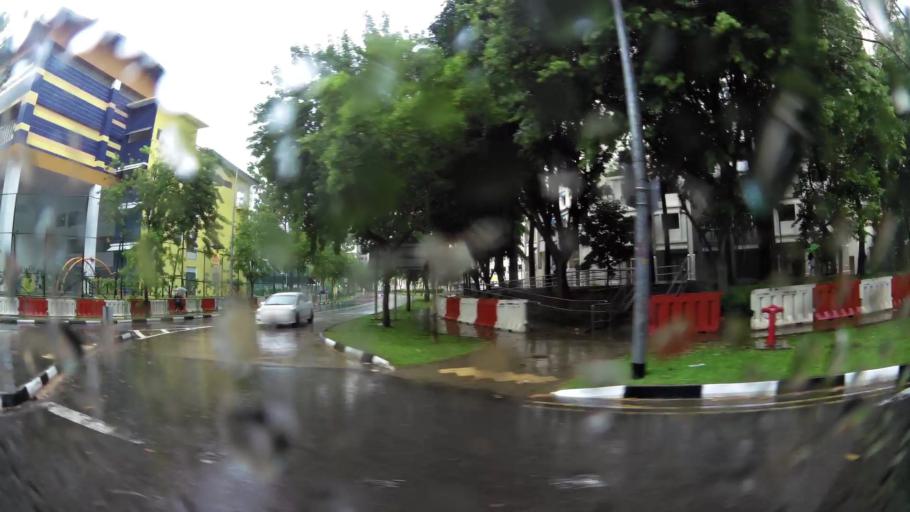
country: MY
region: Johor
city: Kampung Pasir Gudang Baru
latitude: 1.3876
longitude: 103.9047
